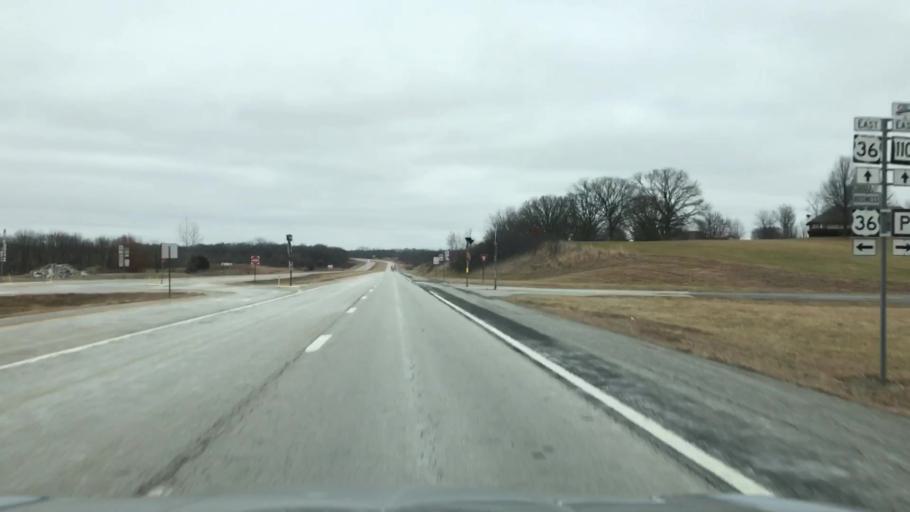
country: US
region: Missouri
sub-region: Caldwell County
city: Hamilton
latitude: 39.7417
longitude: -94.0384
